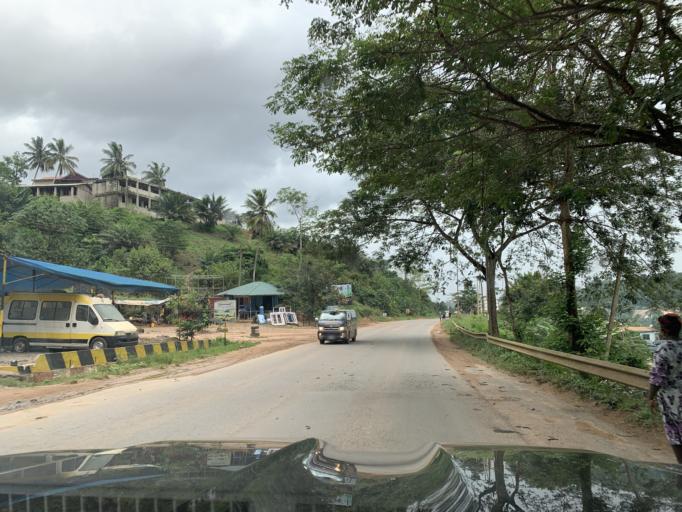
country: GH
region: Western
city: Tarkwa
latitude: 5.3223
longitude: -1.9847
